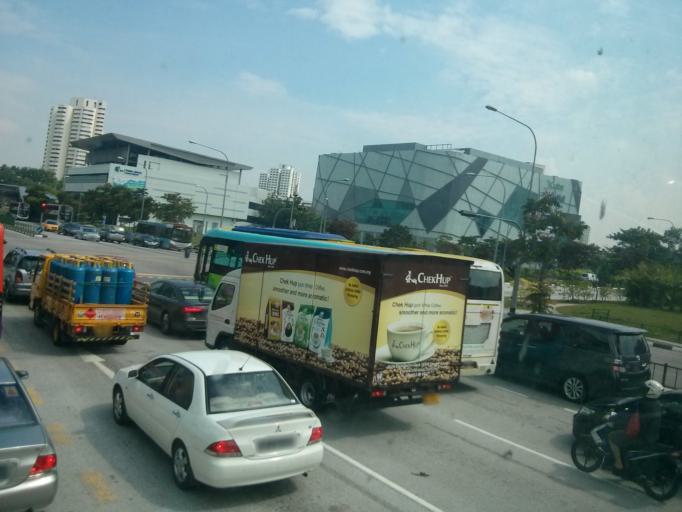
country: SG
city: Singapore
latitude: 1.3311
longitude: 103.7405
